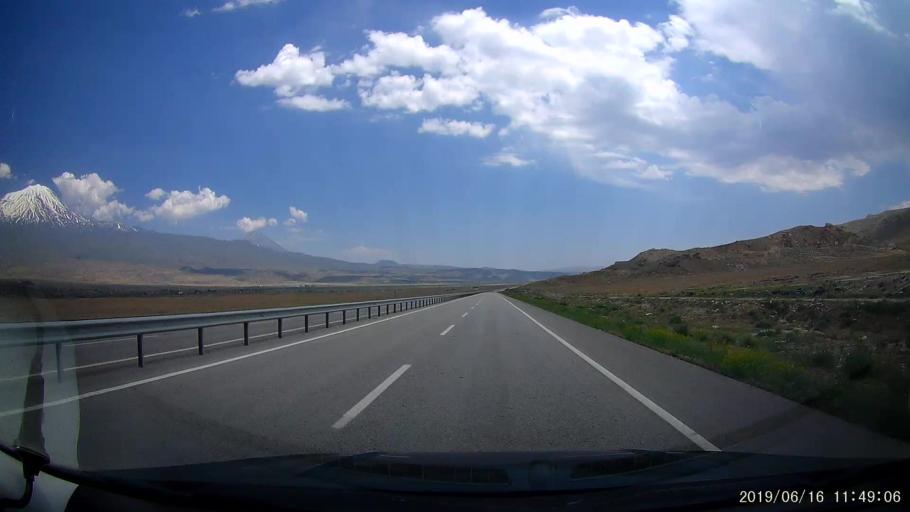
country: TR
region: Agri
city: Dogubayazit
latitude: 39.5577
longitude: 44.1570
